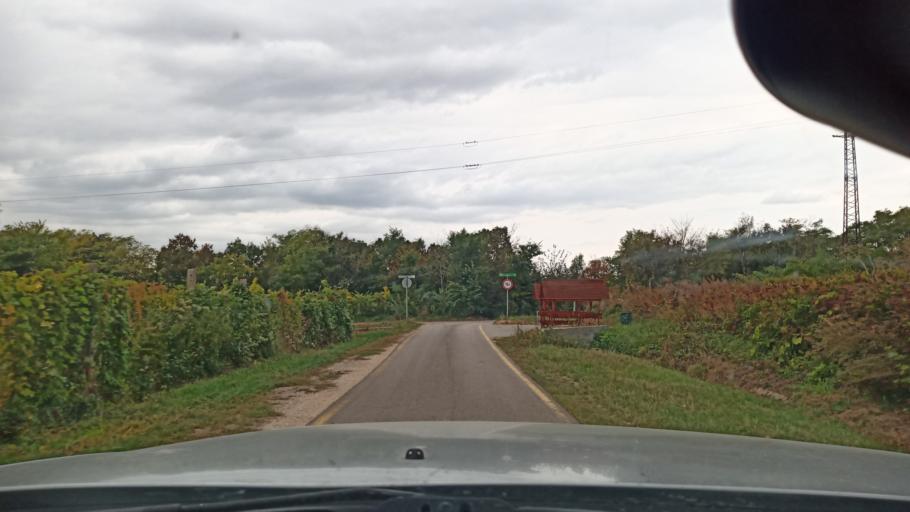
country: HU
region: Fejer
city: Bodajk
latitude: 47.3643
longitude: 18.2496
